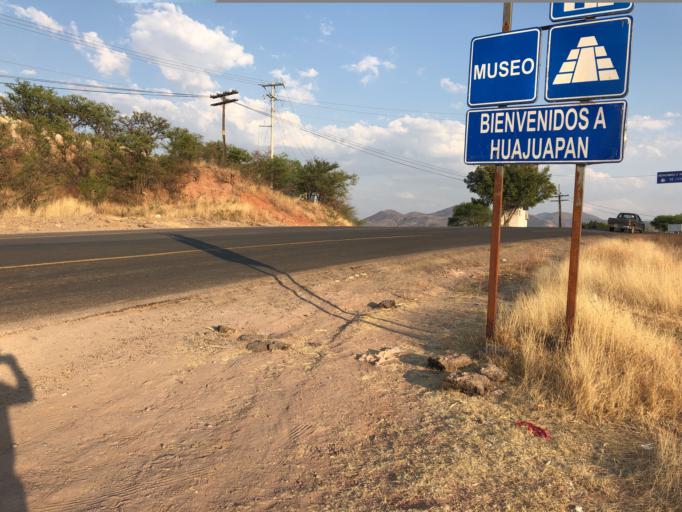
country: MX
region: Oaxaca
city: Ciudad de Huajuapam de Leon
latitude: 17.8351
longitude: -97.7896
